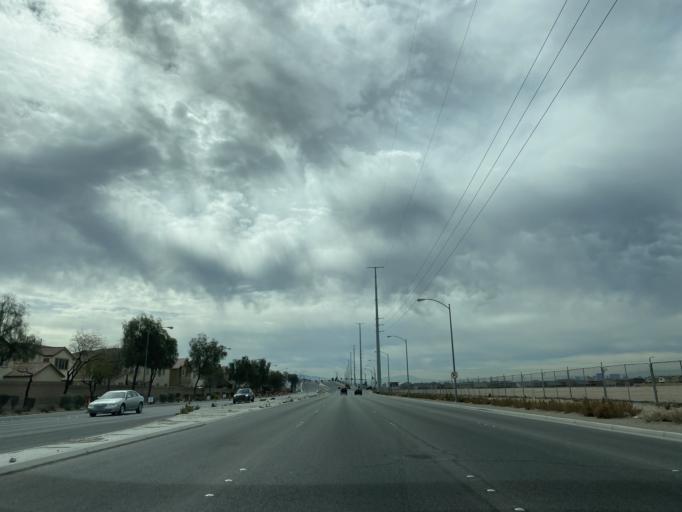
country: US
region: Nevada
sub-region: Clark County
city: Nellis Air Force Base
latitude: 36.2724
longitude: -115.0800
